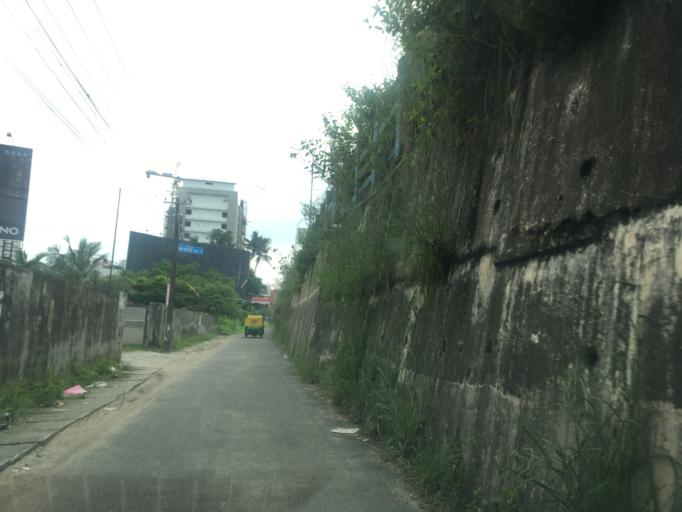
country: IN
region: Kerala
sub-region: Ernakulam
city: Elur
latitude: 10.0325
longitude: 76.3045
